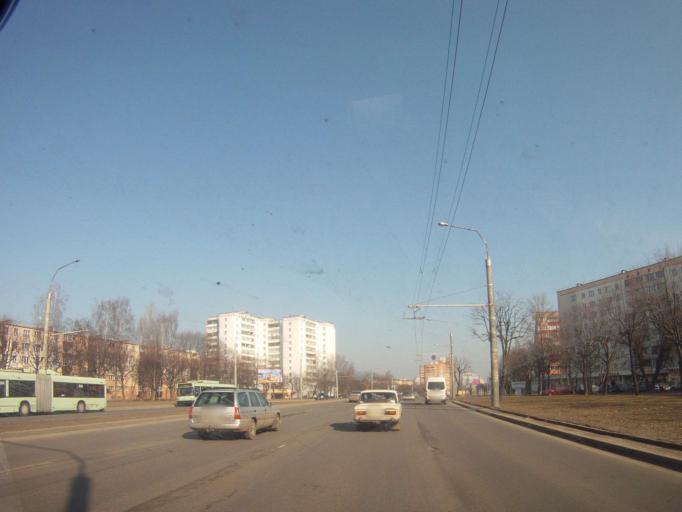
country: BY
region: Minsk
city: Novoye Medvezhino
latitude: 53.9159
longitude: 27.4956
